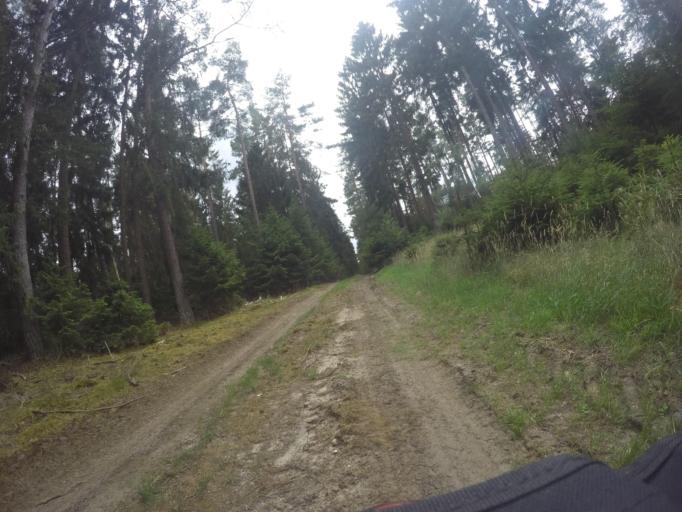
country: DE
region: Lower Saxony
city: Thomasburg
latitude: 53.2422
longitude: 10.6943
